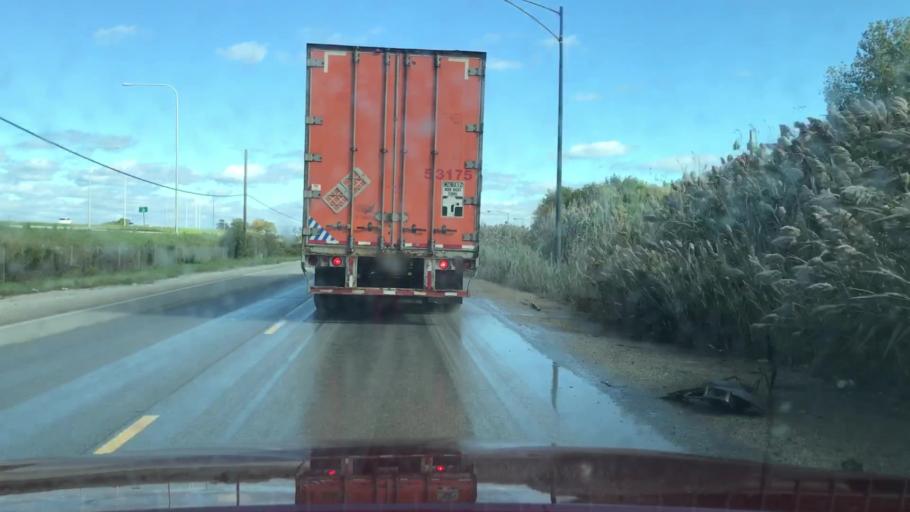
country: US
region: Illinois
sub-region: Cook County
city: Dolton
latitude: 41.7046
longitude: -87.5883
